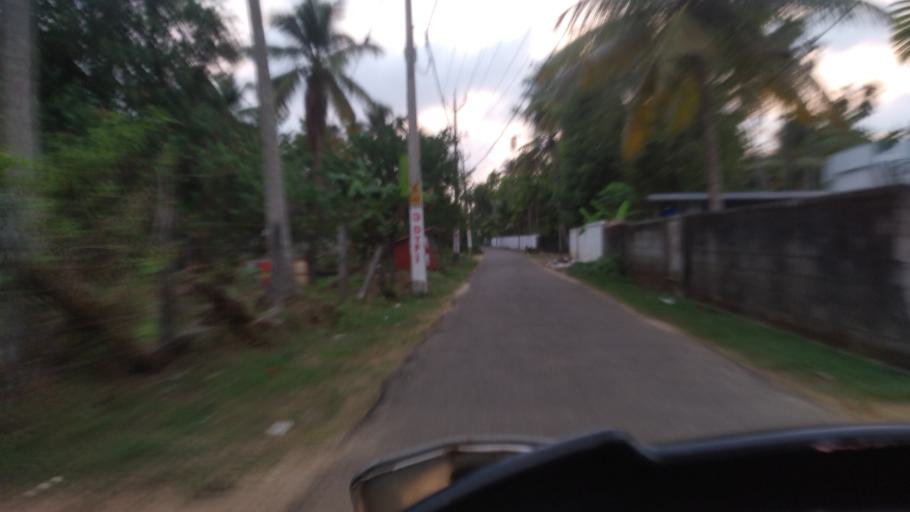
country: IN
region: Kerala
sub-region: Thrissur District
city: Kodungallur
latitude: 10.1462
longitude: 76.2116
